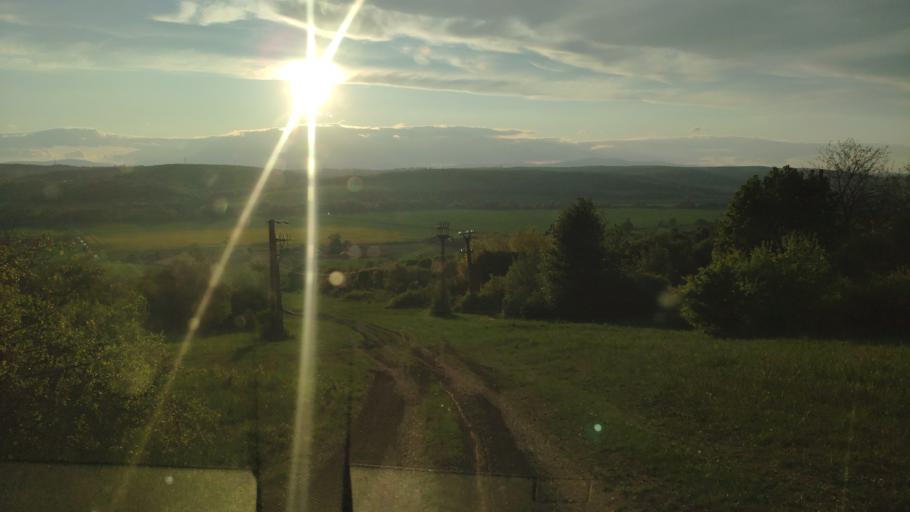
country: SK
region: Kosicky
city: Kosice
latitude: 48.7152
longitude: 21.3540
